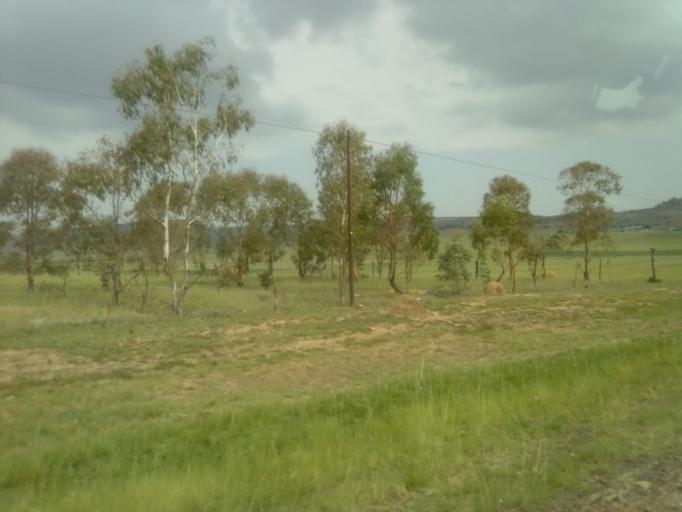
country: LS
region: Berea
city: Teyateyaneng
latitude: -28.9910
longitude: 27.7611
